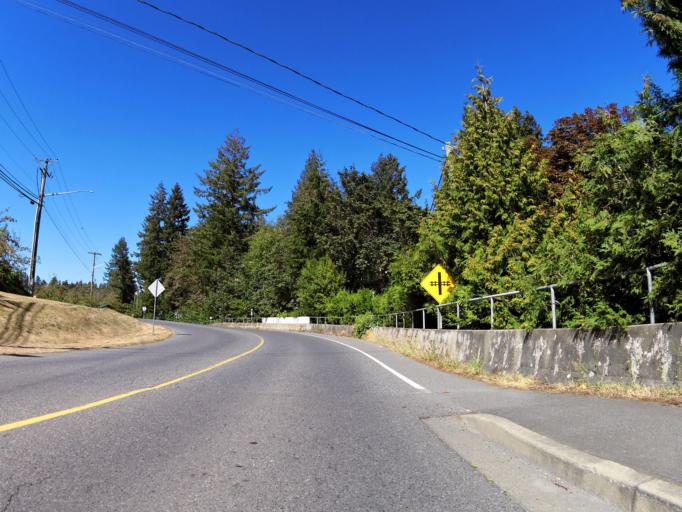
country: CA
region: British Columbia
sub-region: Cowichan Valley Regional District
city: Ladysmith
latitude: 48.9773
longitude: -123.8012
